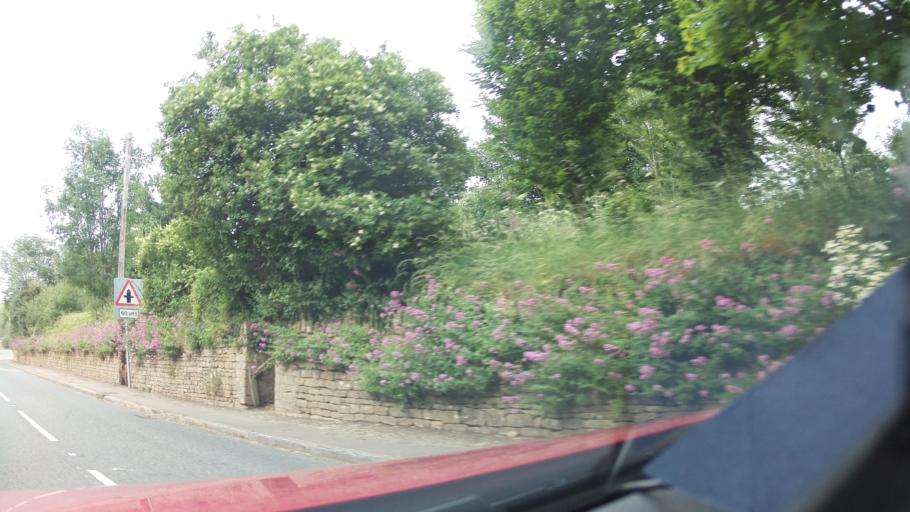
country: GB
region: England
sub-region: Somerset
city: Crewkerne
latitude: 50.8852
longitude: -2.7479
